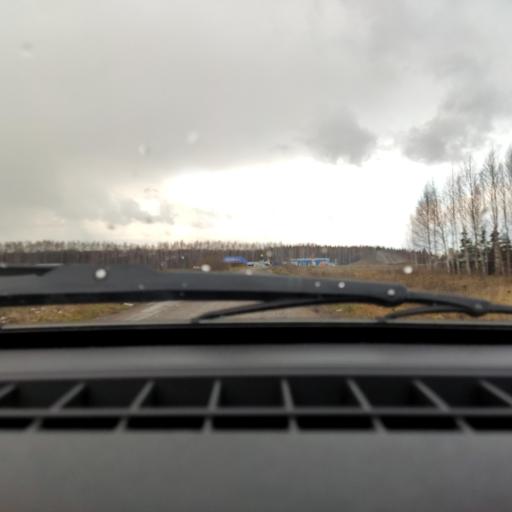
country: RU
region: Bashkortostan
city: Iglino
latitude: 54.7441
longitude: 56.3163
